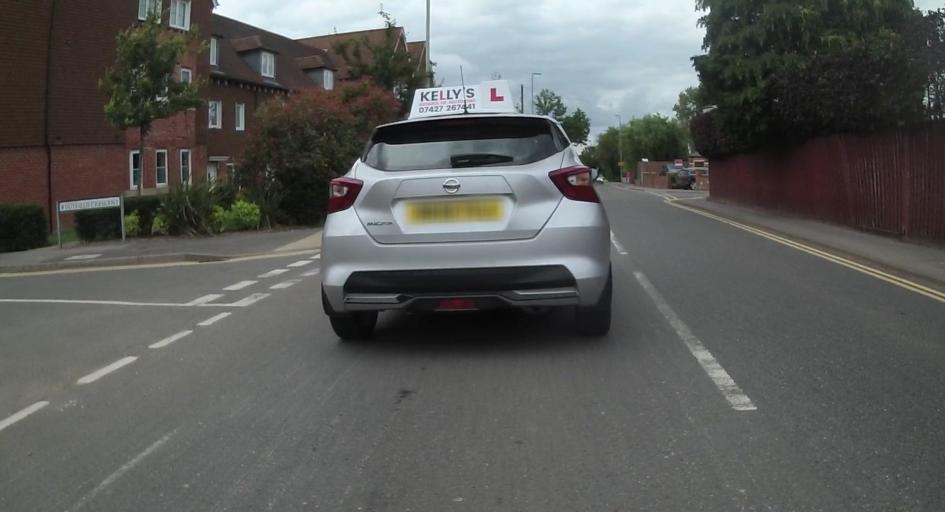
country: GB
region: England
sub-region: Wokingham
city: Wokingham
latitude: 51.4093
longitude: -0.8402
